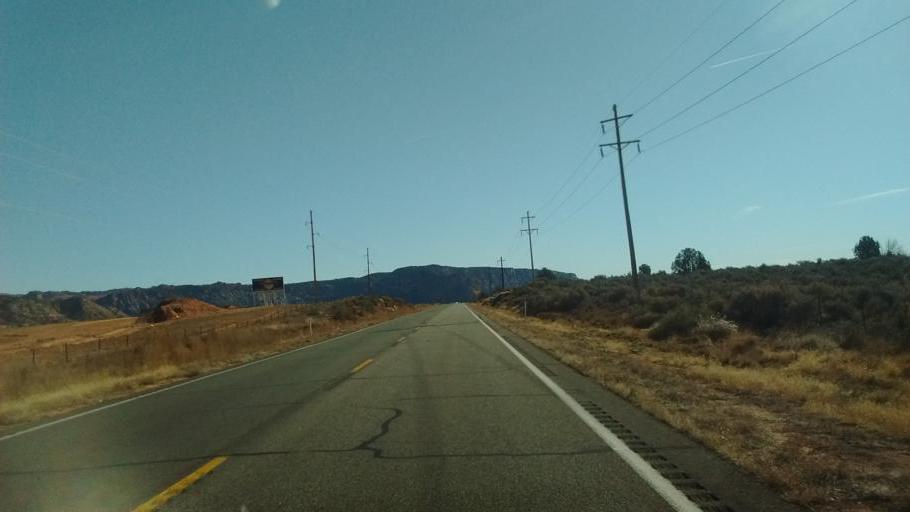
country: US
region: Arizona
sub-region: Mohave County
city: Colorado City
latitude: 37.0099
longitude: -113.0142
